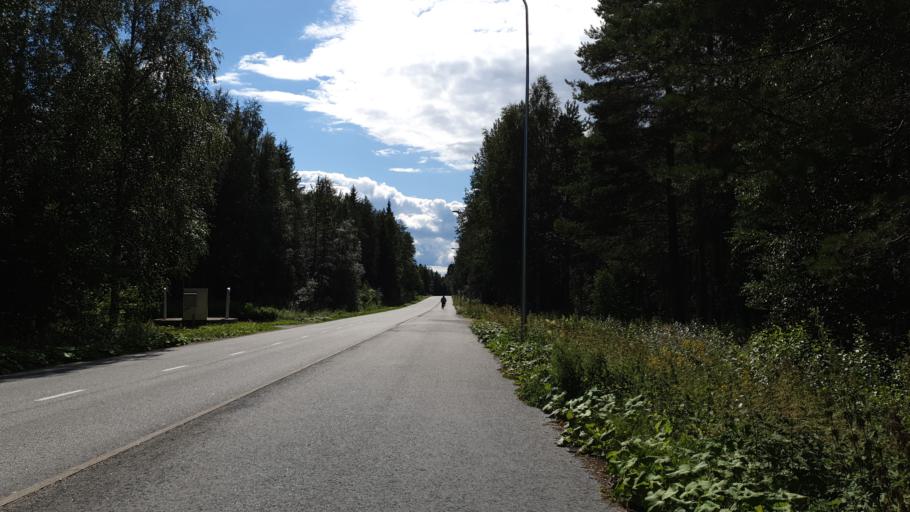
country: FI
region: Kainuu
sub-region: Kehys-Kainuu
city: Kuhmo
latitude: 64.1232
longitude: 29.5016
